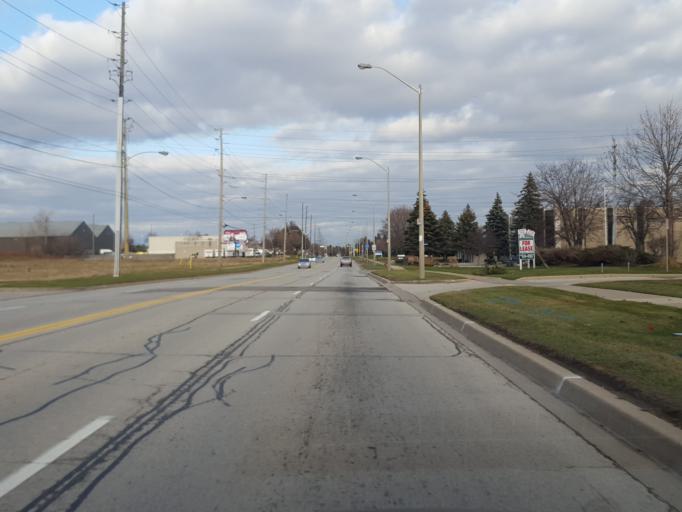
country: CA
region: Ontario
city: Burlington
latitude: 43.3537
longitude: -79.7969
